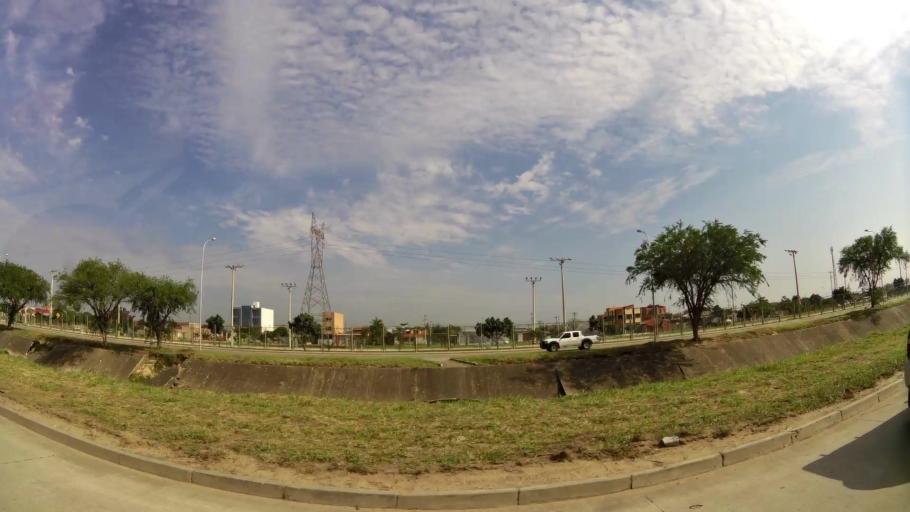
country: BO
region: Santa Cruz
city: Santa Cruz de la Sierra
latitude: -17.7304
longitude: -63.1370
